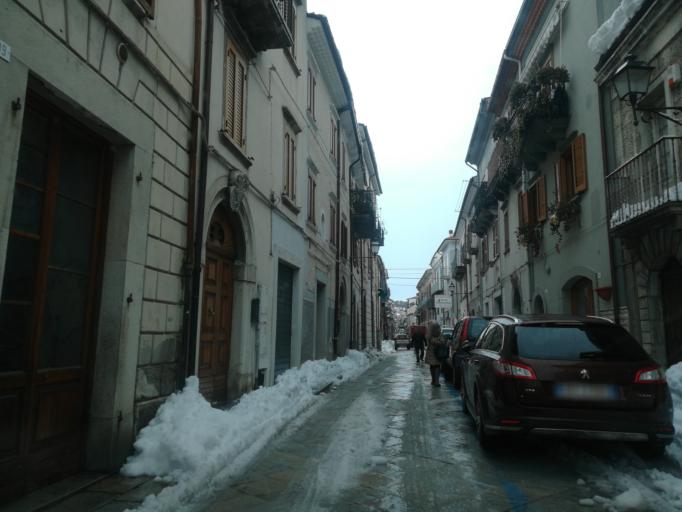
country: IT
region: Molise
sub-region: Provincia di Isernia
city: Agnone
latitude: 41.8066
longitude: 14.3691
